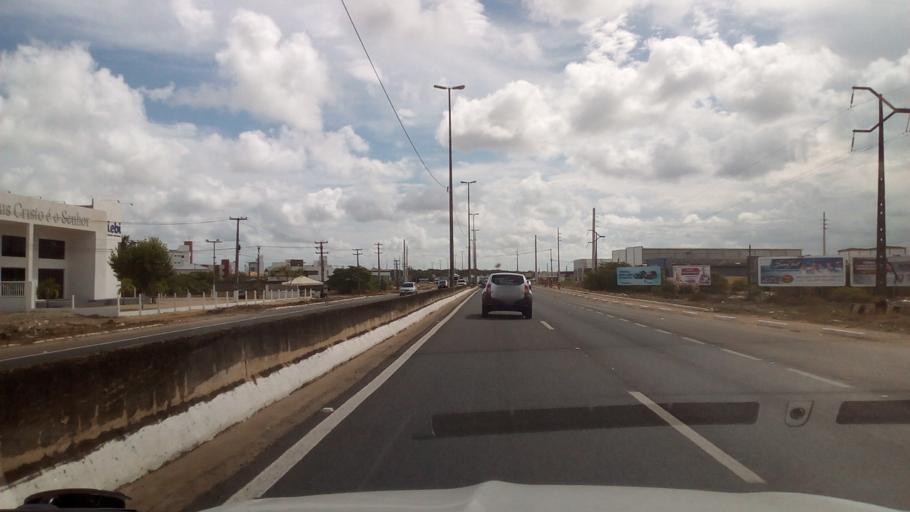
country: BR
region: Paraiba
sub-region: Cabedelo
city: Cabedelo
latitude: -7.0478
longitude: -34.8484
